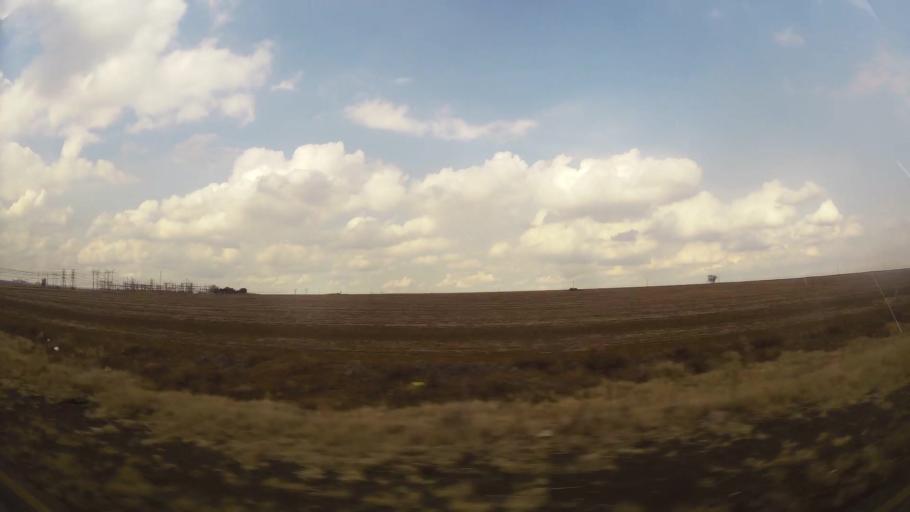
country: ZA
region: Orange Free State
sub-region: Fezile Dabi District Municipality
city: Sasolburg
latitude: -26.8250
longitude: 27.9021
